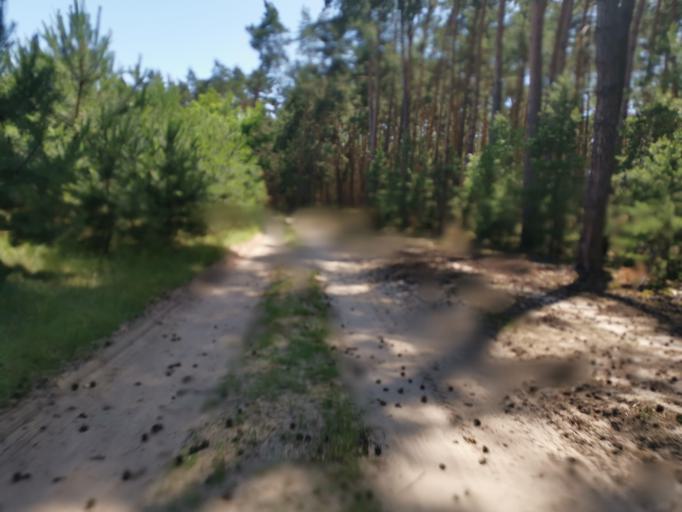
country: CZ
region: South Moravian
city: Vracov
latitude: 48.9636
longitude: 17.2212
